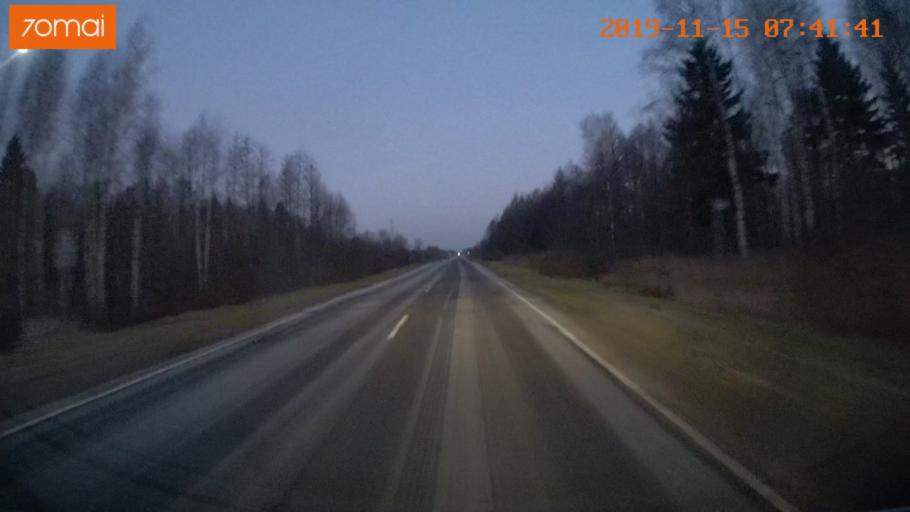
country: RU
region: Vologda
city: Sheksna
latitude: 58.7836
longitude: 38.3538
